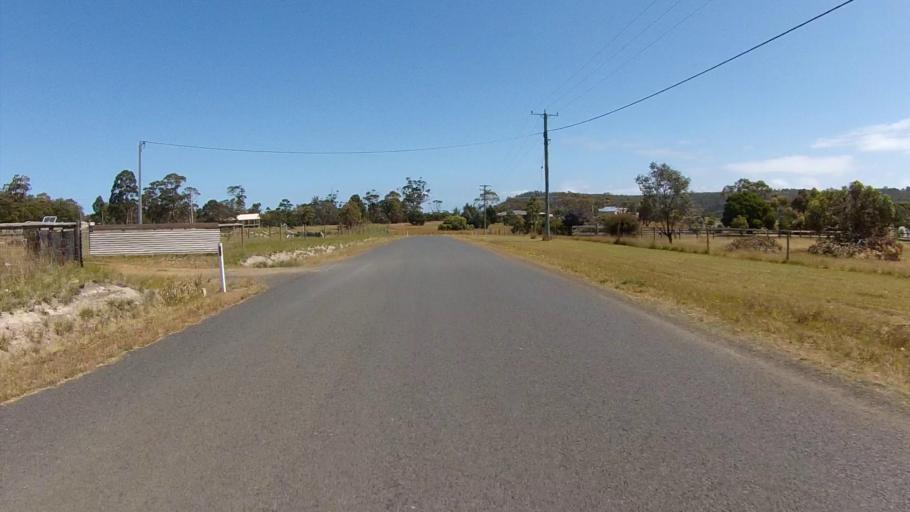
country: AU
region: Tasmania
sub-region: Clarence
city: Sandford
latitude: -42.9560
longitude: 147.4832
